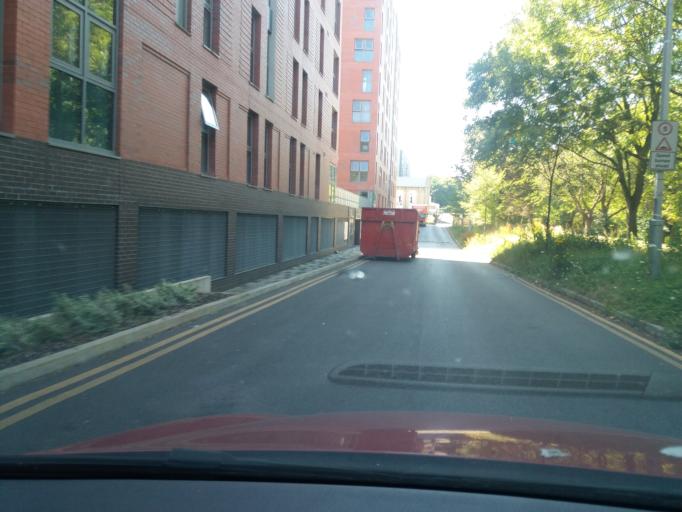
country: GB
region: England
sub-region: City and Borough of Salford
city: Salford
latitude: 53.4898
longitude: -2.2703
